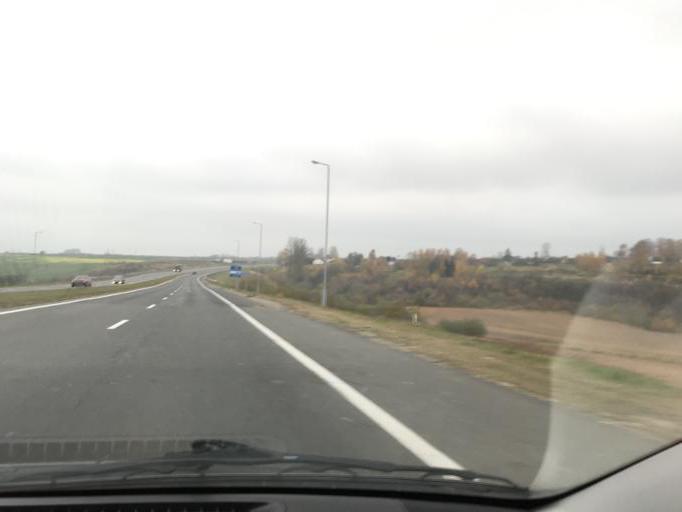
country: BY
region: Vitebsk
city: Vitebsk
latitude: 55.1523
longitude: 30.1222
